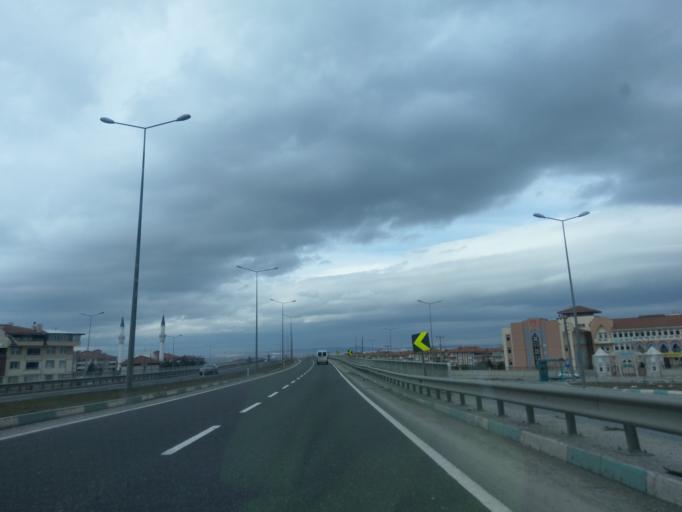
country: TR
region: Kuetahya
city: Kutahya
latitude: 39.4033
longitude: 30.0304
